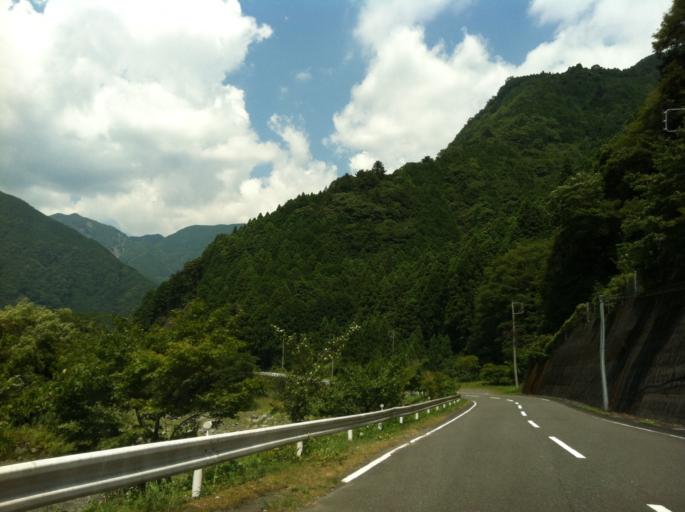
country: JP
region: Shizuoka
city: Shizuoka-shi
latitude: 35.2537
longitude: 138.3355
